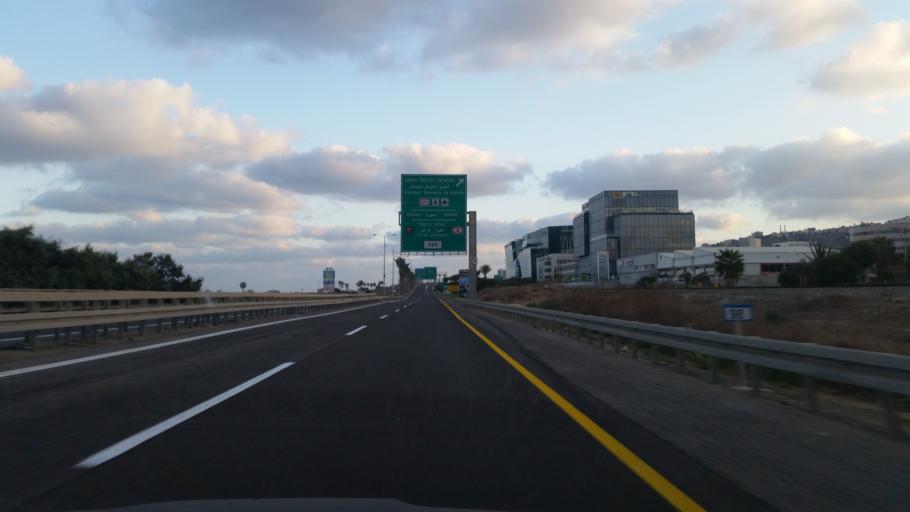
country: IL
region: Haifa
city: Tirat Karmel
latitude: 32.7836
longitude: 34.9565
